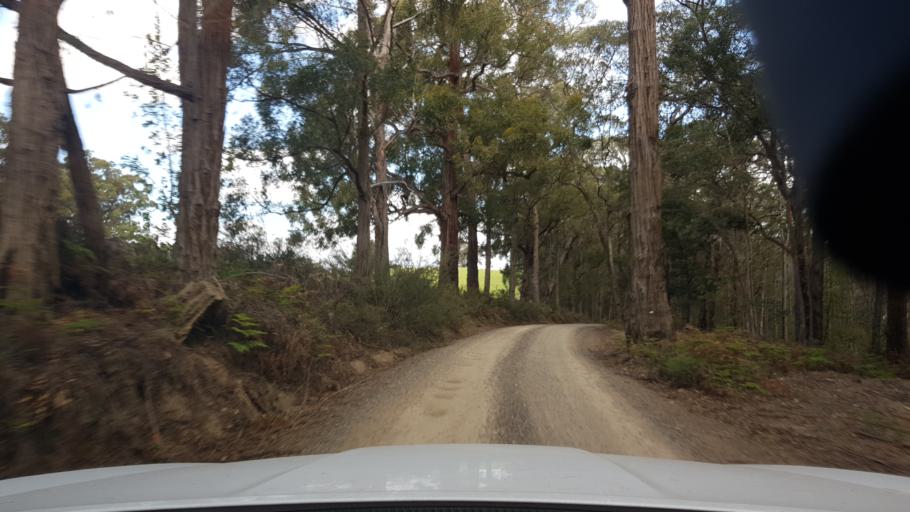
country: AU
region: Victoria
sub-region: East Gippsland
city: Bairnsdale
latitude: -37.7674
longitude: 147.5684
